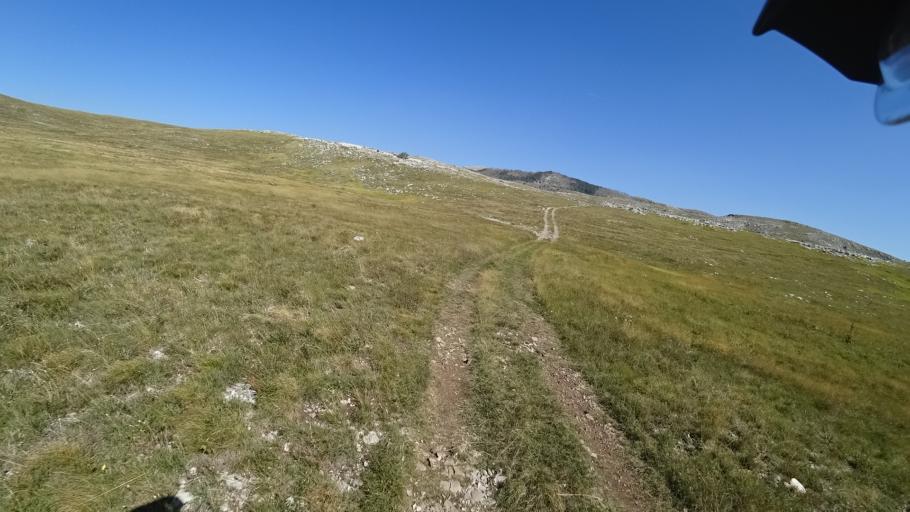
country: HR
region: Splitsko-Dalmatinska
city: Hrvace
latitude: 43.9035
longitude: 16.6070
